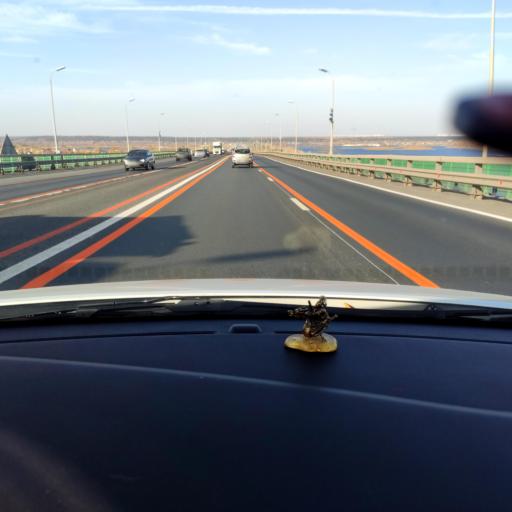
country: RU
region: Tatarstan
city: Osinovo
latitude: 55.7845
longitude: 48.8407
